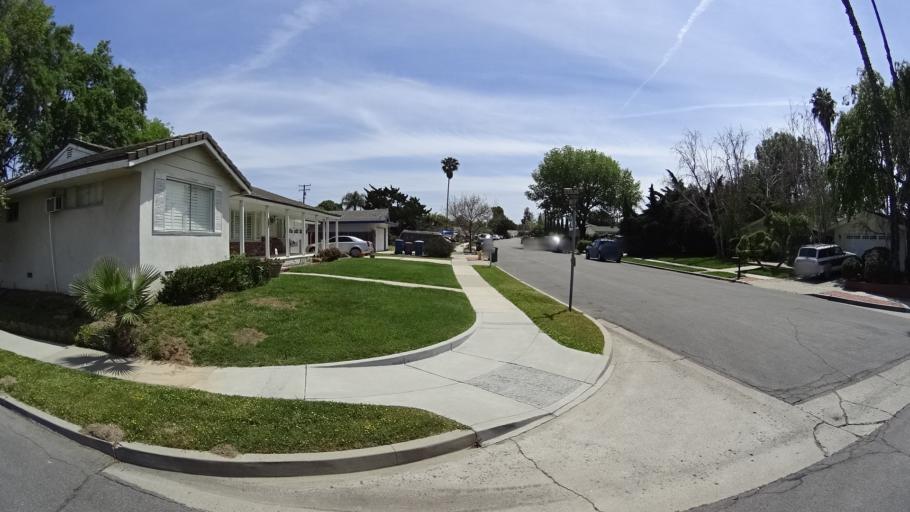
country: US
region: California
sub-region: Ventura County
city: Thousand Oaks
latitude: 34.1948
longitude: -118.8702
